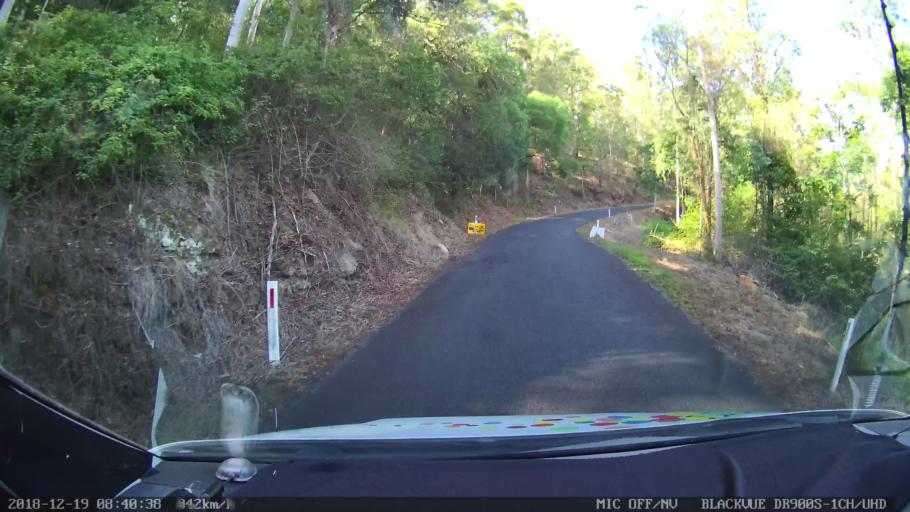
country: AU
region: New South Wales
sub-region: Kyogle
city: Kyogle
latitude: -28.3409
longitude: 152.9689
